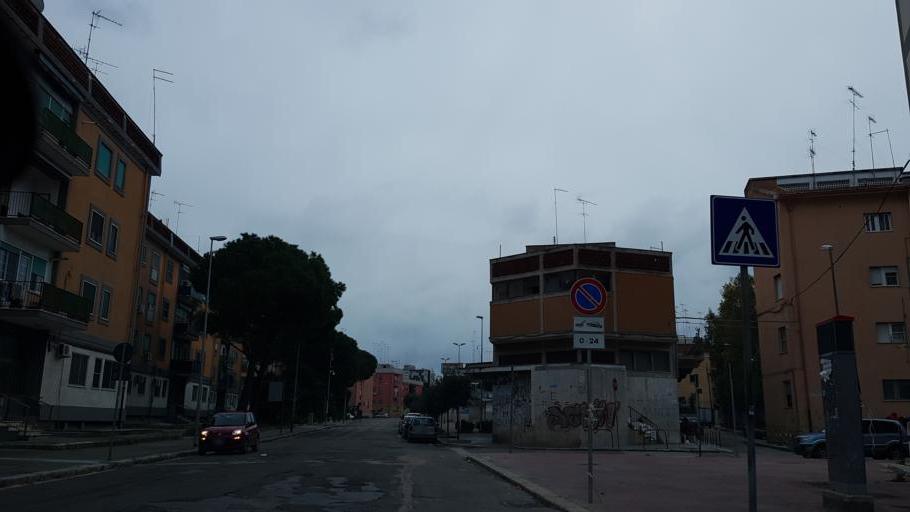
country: IT
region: Apulia
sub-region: Provincia di Brindisi
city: Brindisi
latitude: 40.6280
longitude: 17.9311
